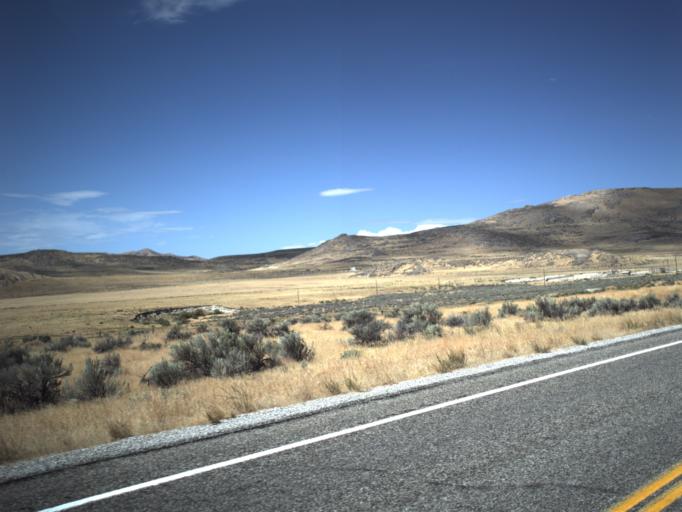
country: US
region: Utah
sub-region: Box Elder County
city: Tremonton
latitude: 41.6539
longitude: -112.4392
